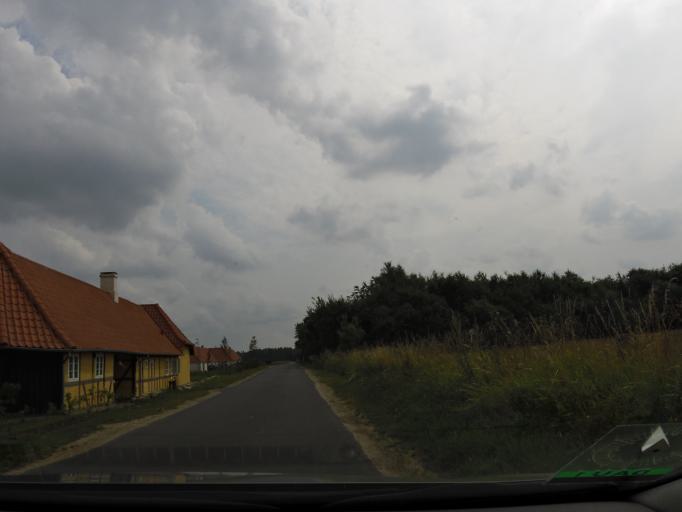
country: DK
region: South Denmark
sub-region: Odense Kommune
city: Neder Holluf
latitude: 55.3847
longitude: 10.4712
